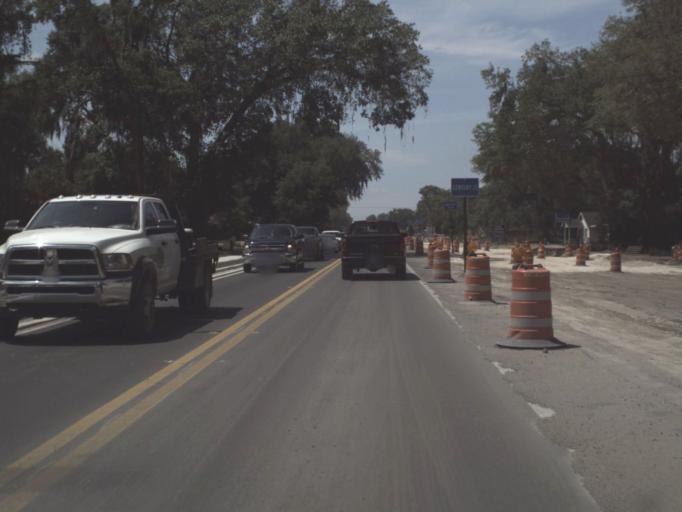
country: US
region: Florida
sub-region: Sumter County
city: Bushnell
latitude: 28.6686
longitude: -82.1209
